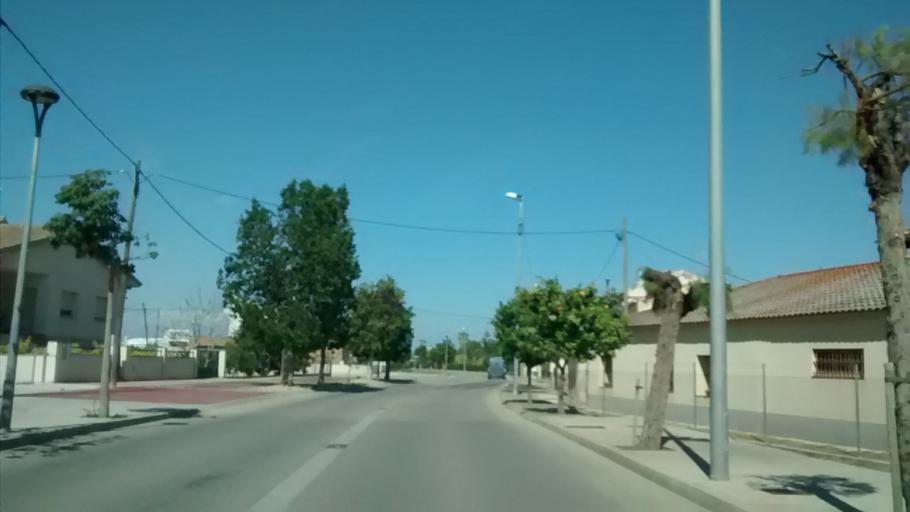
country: ES
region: Catalonia
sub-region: Provincia de Tarragona
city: Deltebre
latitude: 40.7161
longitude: 0.7193
